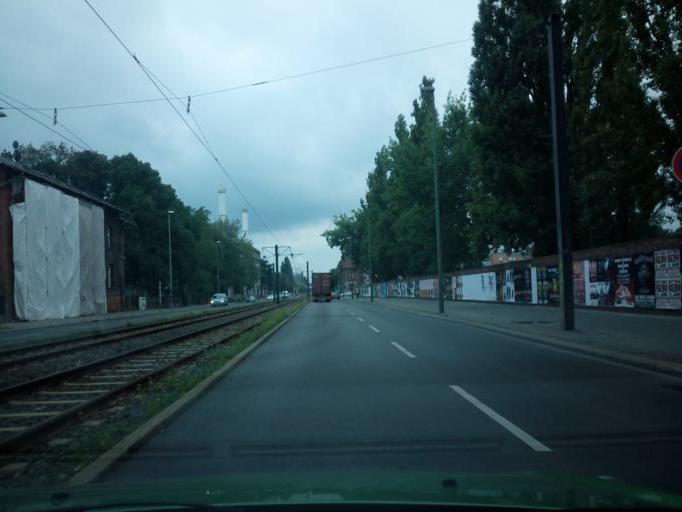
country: DE
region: Berlin
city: Rummelsburg
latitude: 52.4950
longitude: 13.4886
